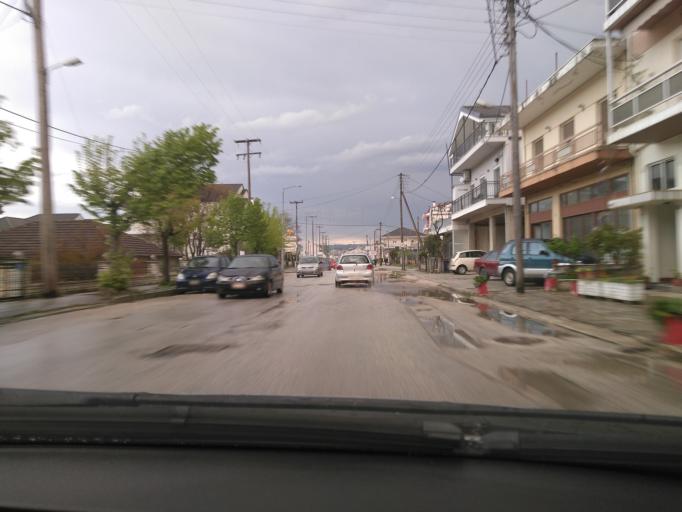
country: GR
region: Epirus
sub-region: Nomos Ioanninon
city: Anatoli
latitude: 39.6384
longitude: 20.8694
